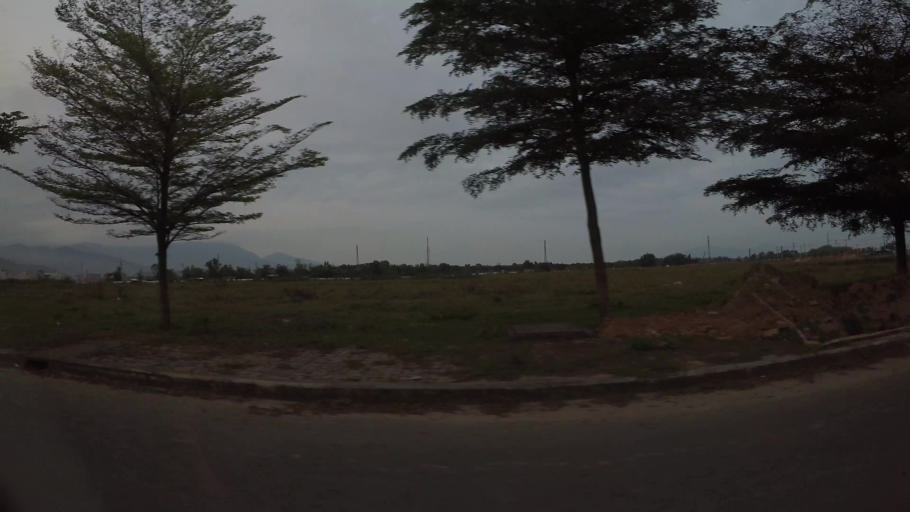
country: VN
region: Da Nang
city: Lien Chieu
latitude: 16.0895
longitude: 108.1096
